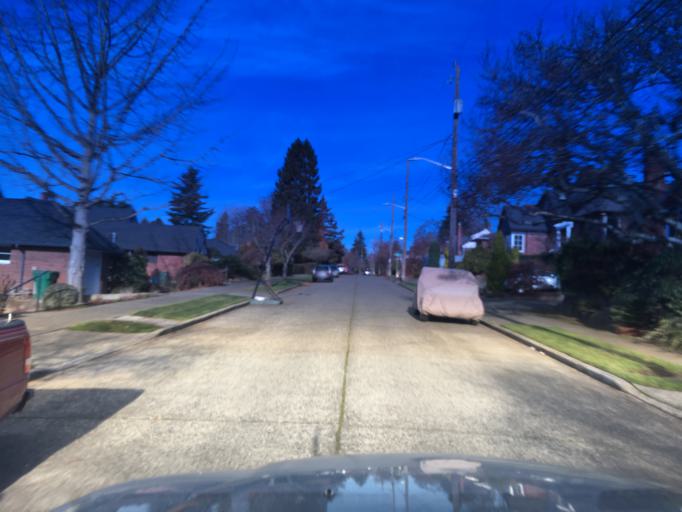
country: US
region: Washington
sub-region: King County
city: Inglewood-Finn Hill
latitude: 47.6769
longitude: -122.2780
